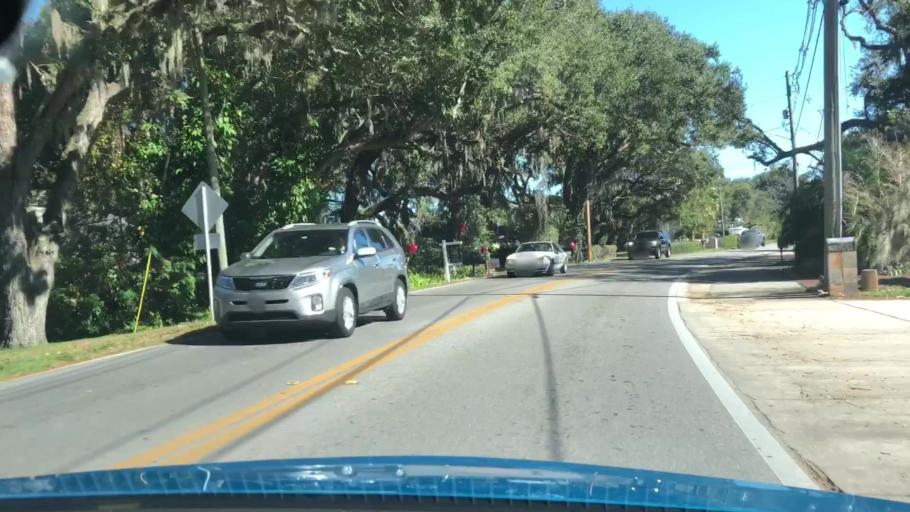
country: US
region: Florida
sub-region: Orange County
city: Pine Castle
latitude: 28.4847
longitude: -81.3513
